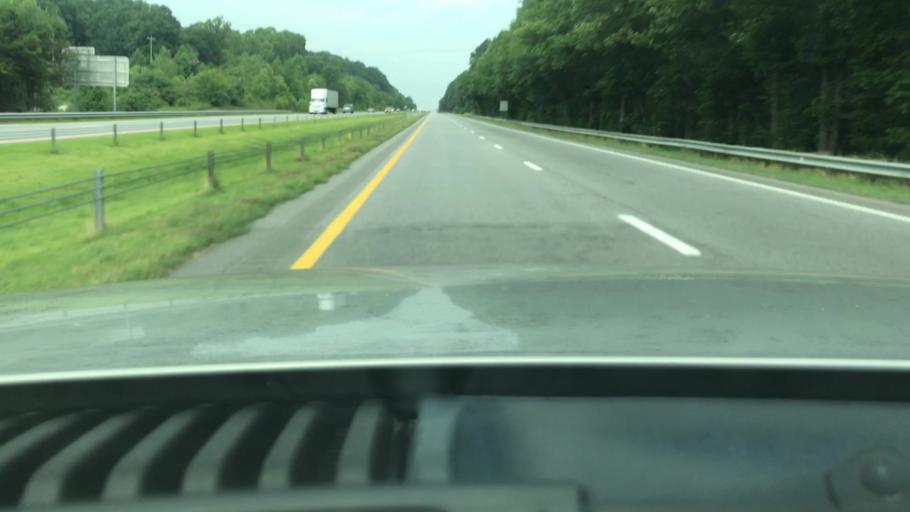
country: US
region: North Carolina
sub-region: Wilkes County
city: North Wilkesboro
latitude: 36.1493
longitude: -81.0287
